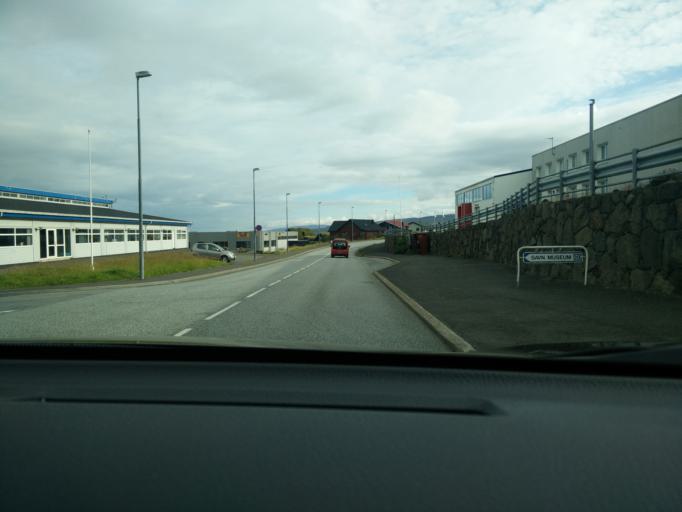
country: FO
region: Streymoy
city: Hoyvik
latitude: 62.0330
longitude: -6.7664
